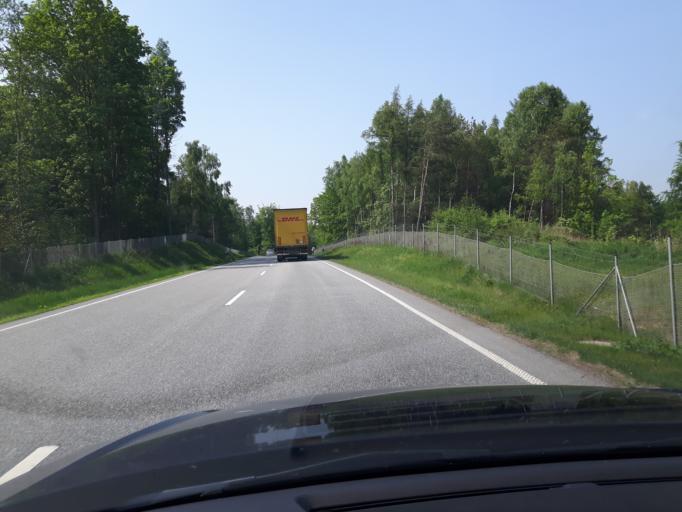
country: DE
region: Schleswig-Holstein
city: Ratekau
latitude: 53.8810
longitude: 10.7708
